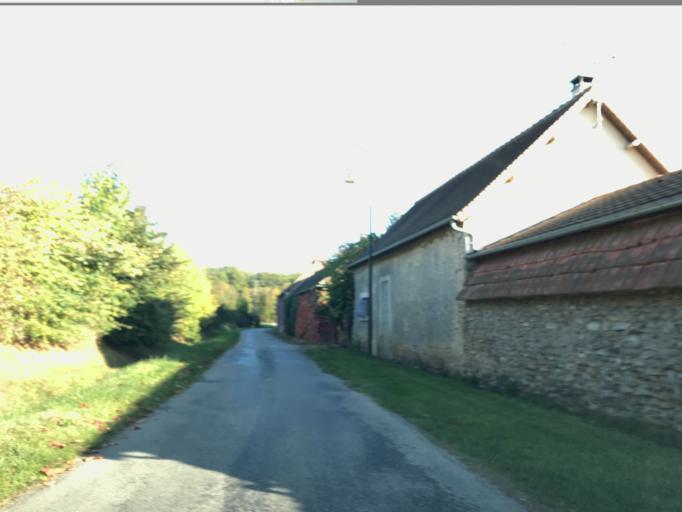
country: FR
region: Haute-Normandie
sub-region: Departement de l'Eure
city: Saint-Aubin-sur-Gaillon
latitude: 49.0766
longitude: 1.2641
